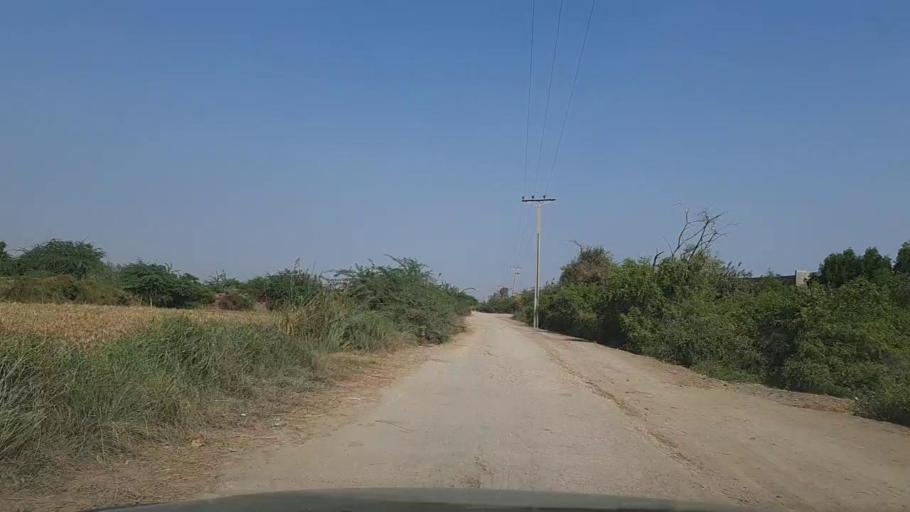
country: PK
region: Sindh
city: Thatta
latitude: 24.5938
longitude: 67.9492
